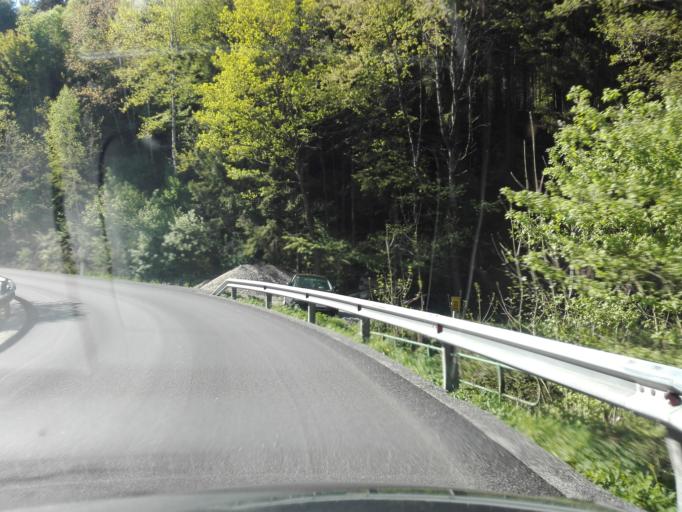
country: DE
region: Bavaria
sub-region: Lower Bavaria
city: Obernzell
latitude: 48.4456
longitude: 13.6445
